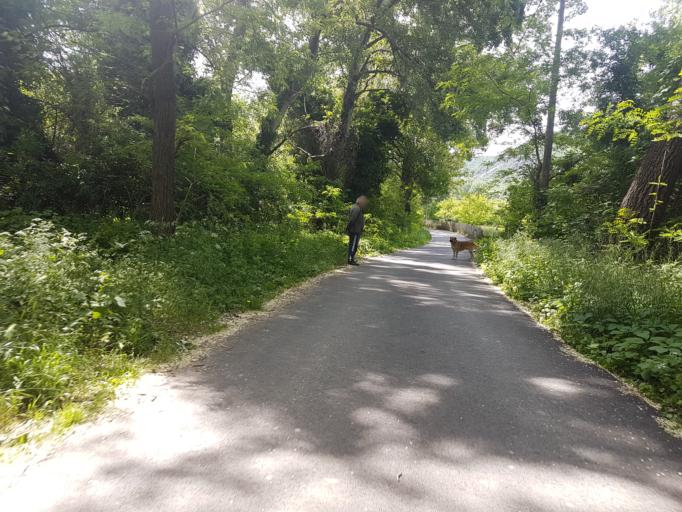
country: FR
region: Rhone-Alpes
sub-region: Departement de la Drome
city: Saulce-sur-Rhone
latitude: 44.7080
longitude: 4.7676
